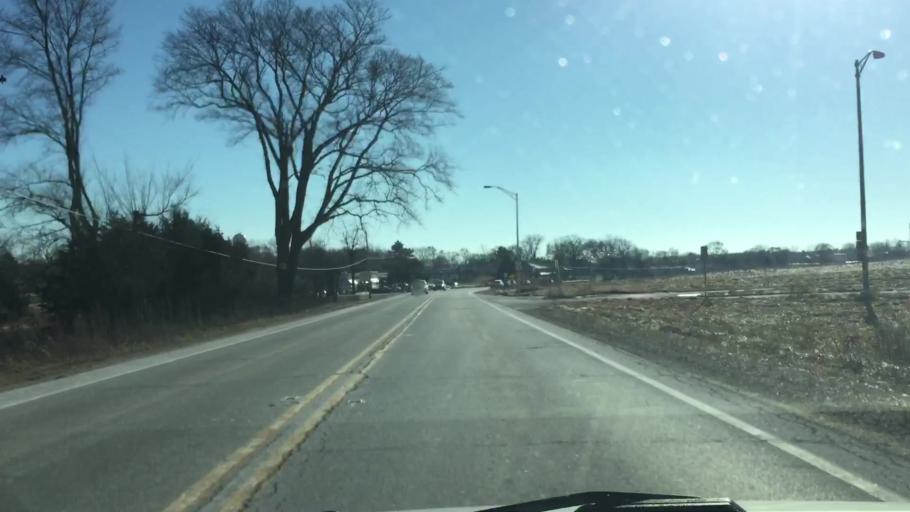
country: US
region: Illinois
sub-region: McHenry County
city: Richmond
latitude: 42.4916
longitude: -88.3083
